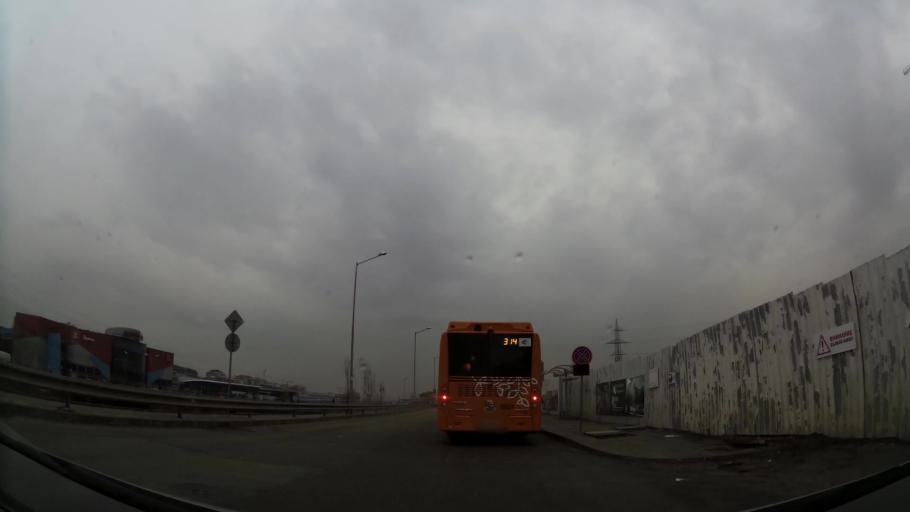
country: BG
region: Sofia-Capital
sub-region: Stolichna Obshtina
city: Sofia
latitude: 42.6230
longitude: 23.3749
